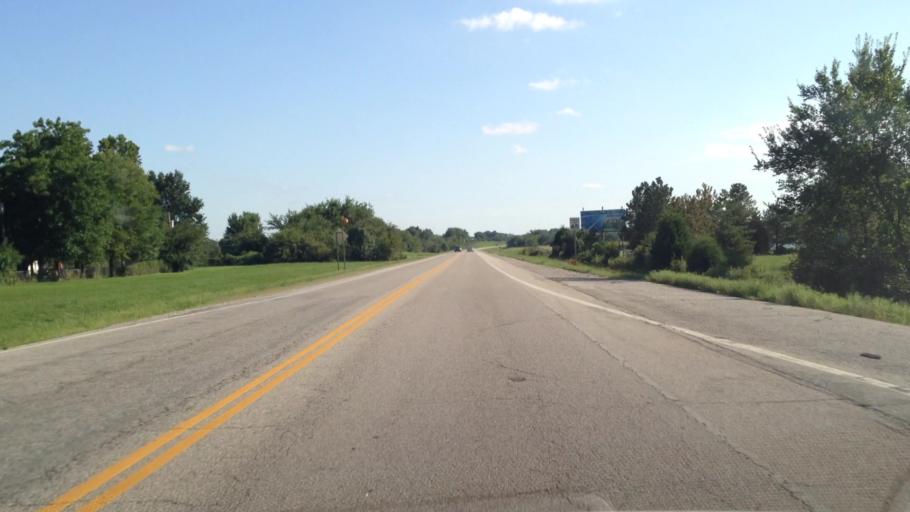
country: US
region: Kansas
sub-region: Crawford County
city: Arma
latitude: 37.5415
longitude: -94.7102
